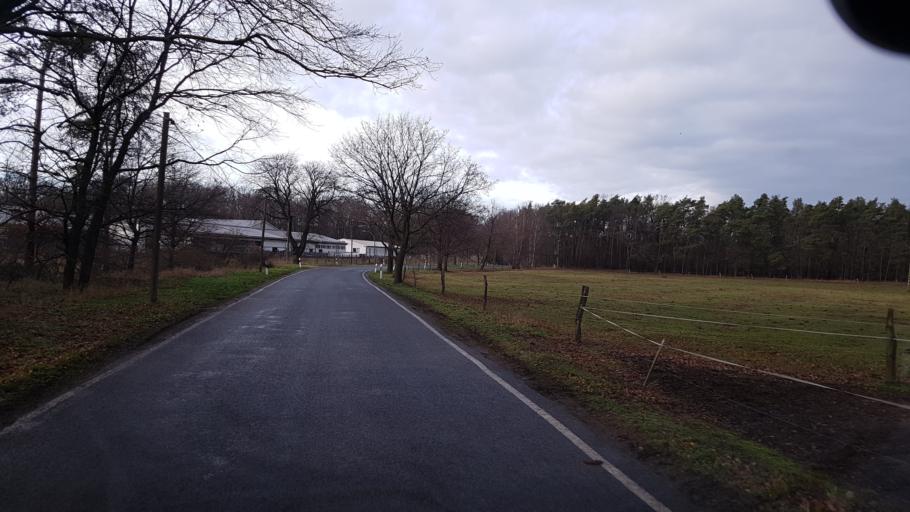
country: DE
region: Brandenburg
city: Altdobern
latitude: 51.6678
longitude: 13.9885
